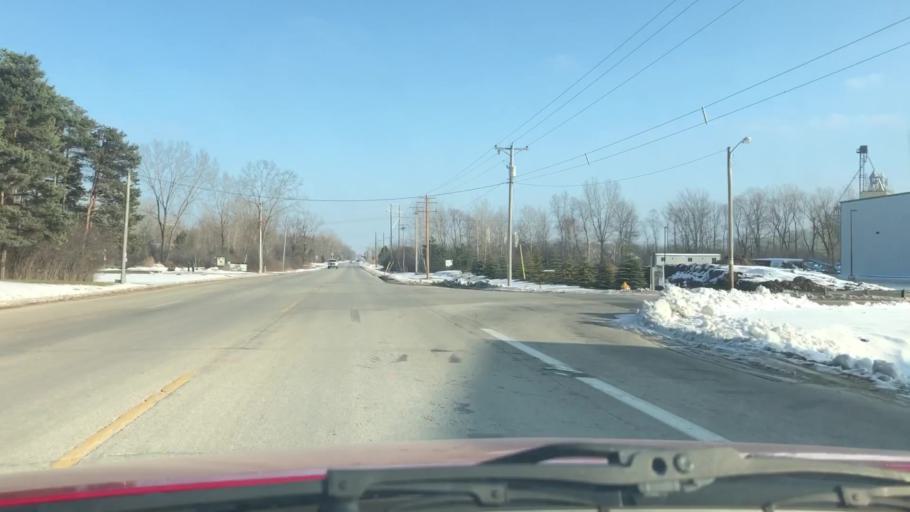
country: US
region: Wisconsin
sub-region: Outagamie County
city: Appleton
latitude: 44.3169
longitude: -88.4402
